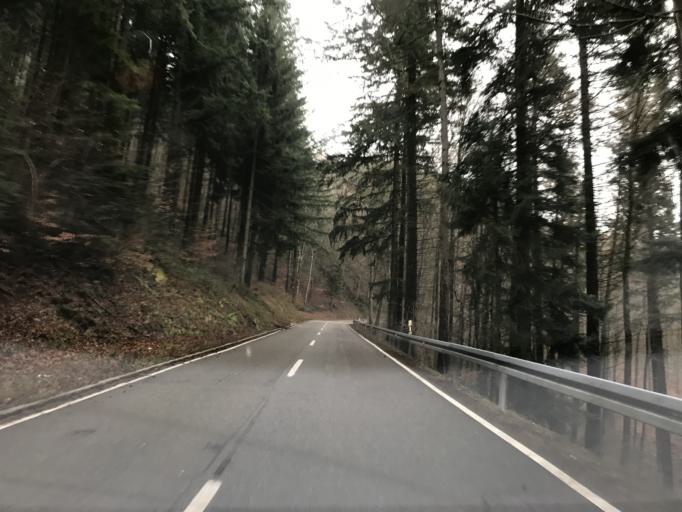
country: DE
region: Baden-Wuerttemberg
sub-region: Freiburg Region
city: Wehr
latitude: 47.6162
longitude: 7.9346
